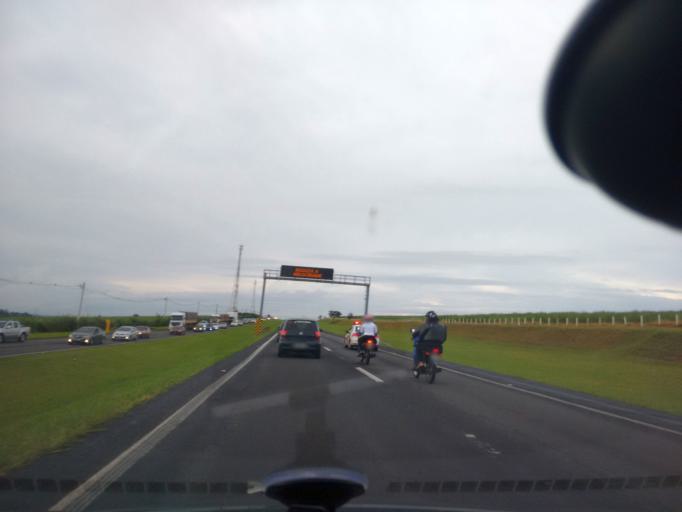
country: BR
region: Sao Paulo
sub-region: Itirapina
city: Itirapina
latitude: -22.1967
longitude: -47.7748
